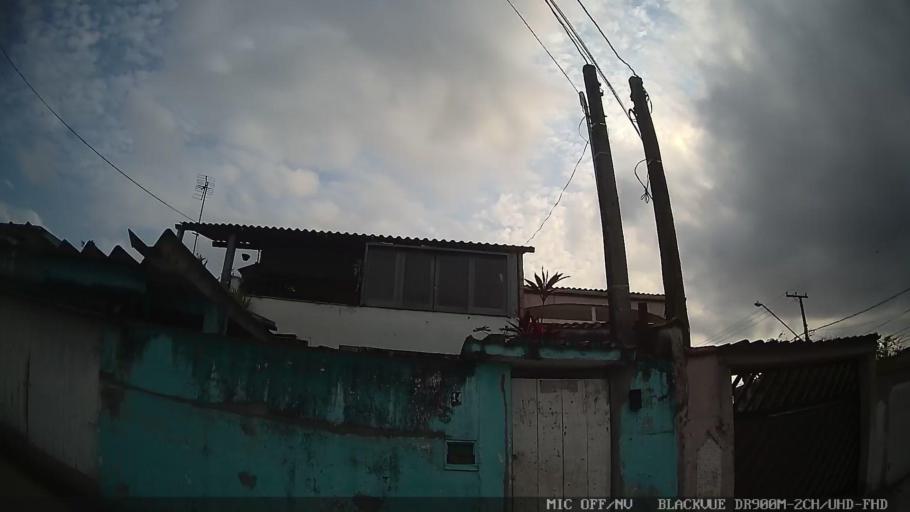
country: BR
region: Sao Paulo
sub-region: Guaruja
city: Guaruja
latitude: -23.9559
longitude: -46.2811
